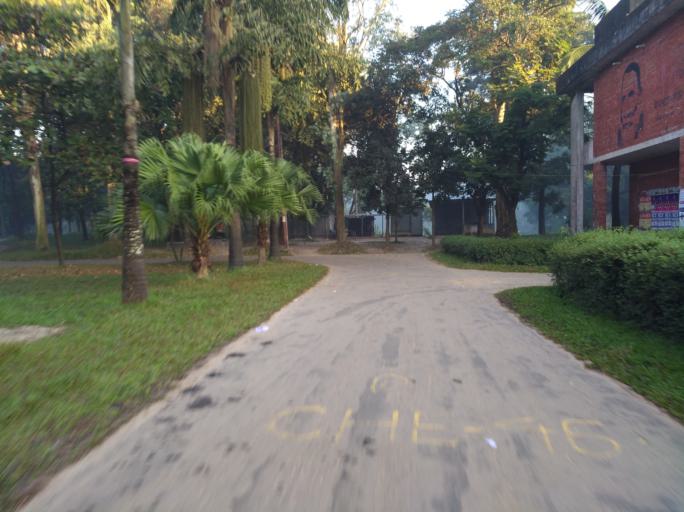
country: BD
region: Dhaka
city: Tungi
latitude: 23.8760
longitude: 90.2714
